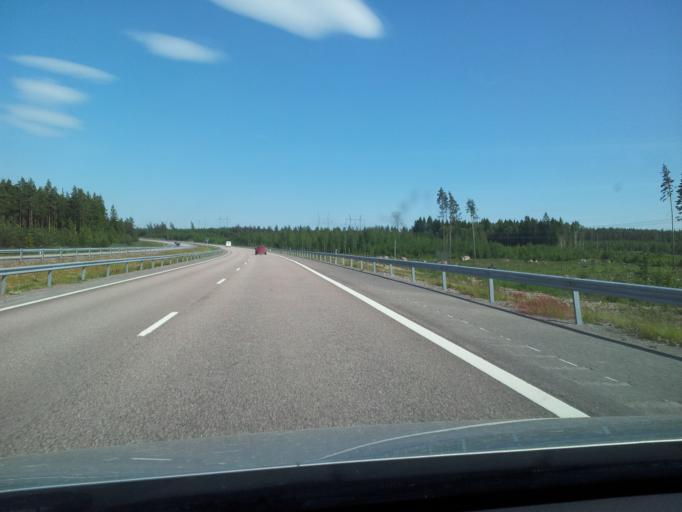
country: FI
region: Uusimaa
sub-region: Loviisa
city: Perna
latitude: 60.4780
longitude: 26.0439
